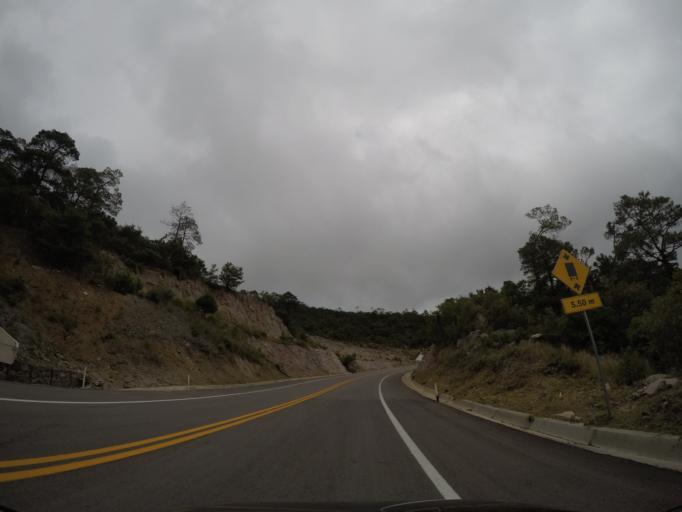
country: MX
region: Oaxaca
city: San Lorenzo Albarradas
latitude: 16.9368
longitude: -96.2744
